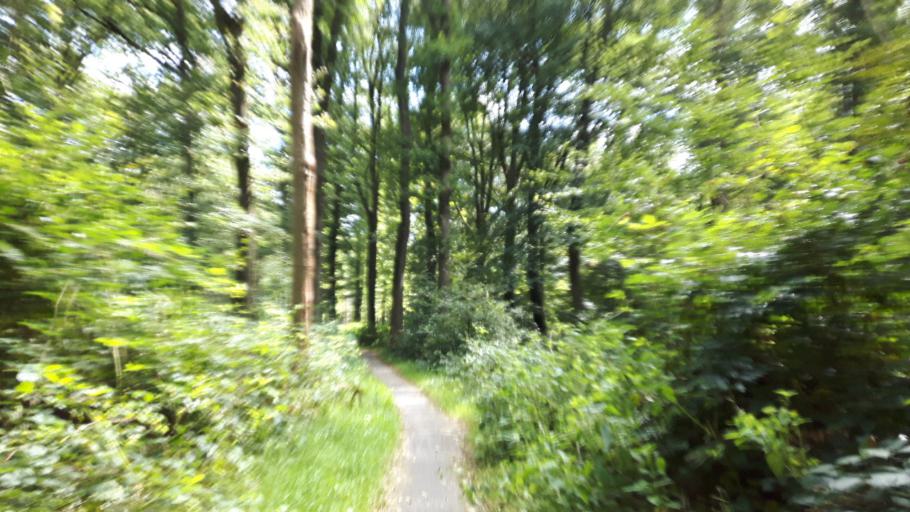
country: NL
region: Friesland
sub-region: Gemeente Smallingerland
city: Drachtstercompagnie
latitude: 53.0689
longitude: 6.2064
